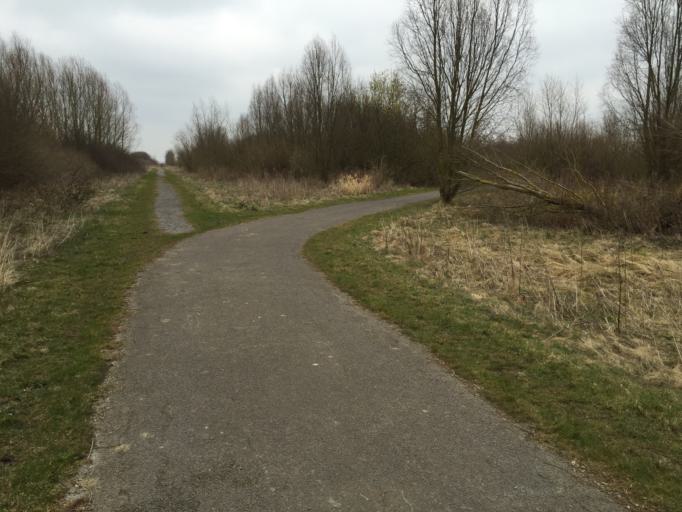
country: NL
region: South Holland
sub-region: Gemeente Hillegom
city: Hillegom
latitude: 52.2722
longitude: 4.5826
